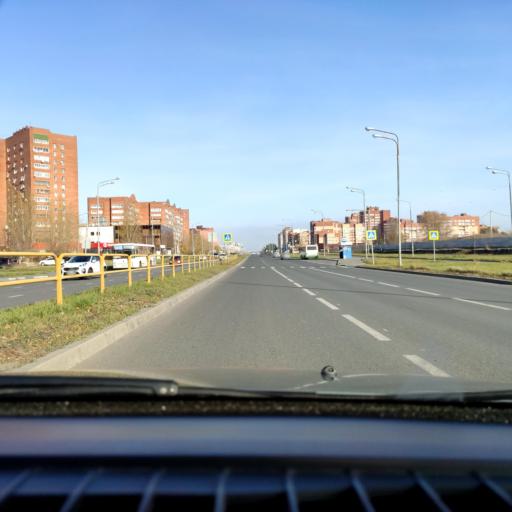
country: RU
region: Samara
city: Tol'yatti
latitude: 53.5331
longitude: 49.3468
